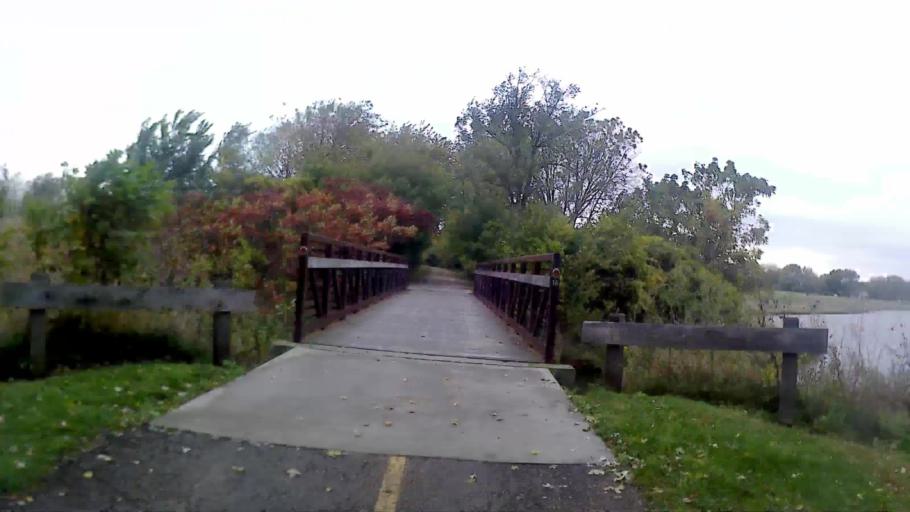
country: US
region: Illinois
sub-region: Kane County
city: Montgomery
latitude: 41.7558
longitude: -88.3819
